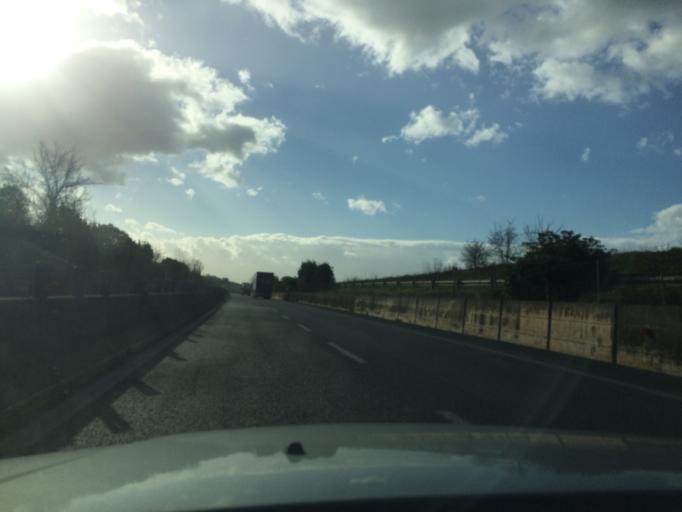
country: IT
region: Umbria
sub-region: Provincia di Perugia
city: Collepepe
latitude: 42.9159
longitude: 12.3917
